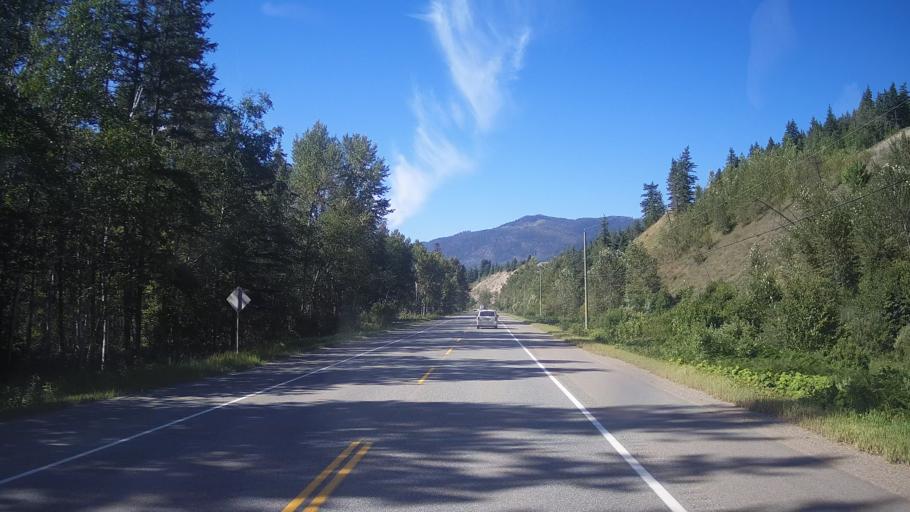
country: CA
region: British Columbia
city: Kamloops
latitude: 51.4440
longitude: -120.1875
